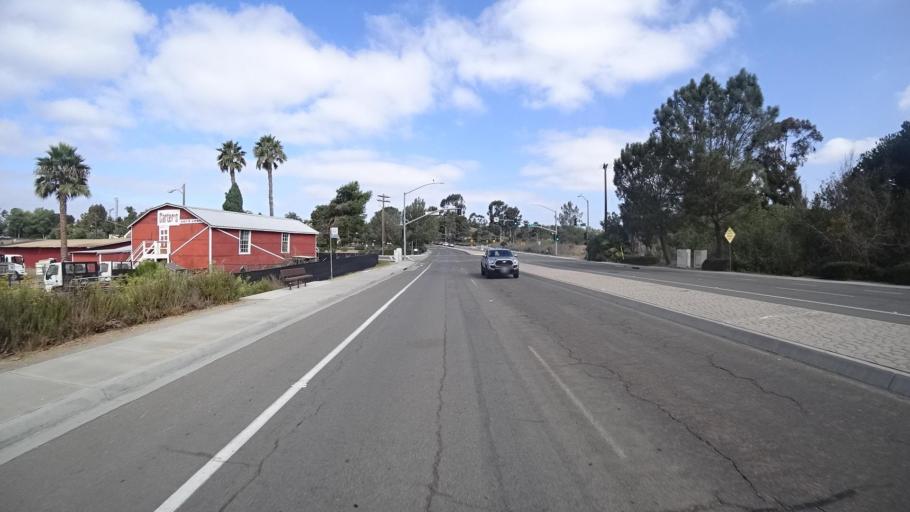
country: US
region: California
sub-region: San Diego County
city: Encinitas
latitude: 33.0672
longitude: -117.2455
